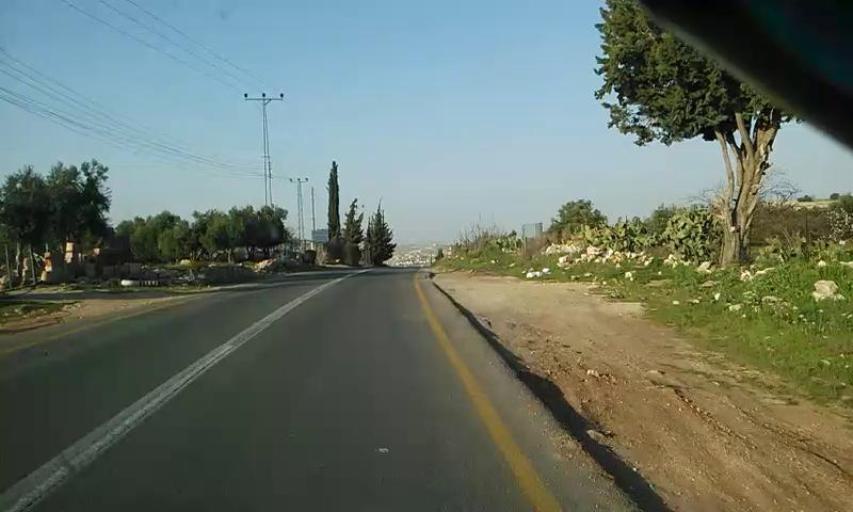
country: PS
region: West Bank
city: Marah Rabbah
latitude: 31.6468
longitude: 35.2027
